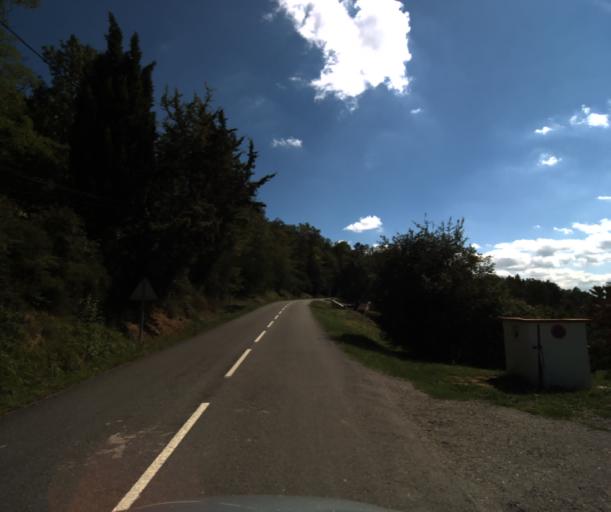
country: FR
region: Midi-Pyrenees
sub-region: Departement de la Haute-Garonne
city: Le Fauga
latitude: 43.4120
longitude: 1.3138
